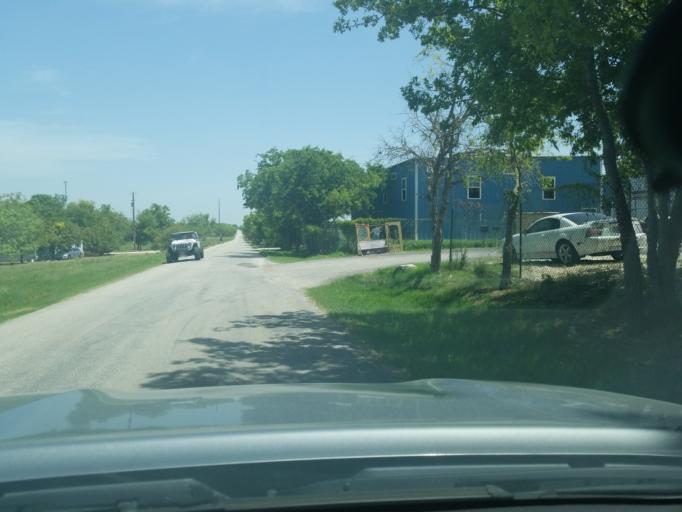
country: US
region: Texas
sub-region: Guadalupe County
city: Cibolo
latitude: 29.5860
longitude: -98.2020
